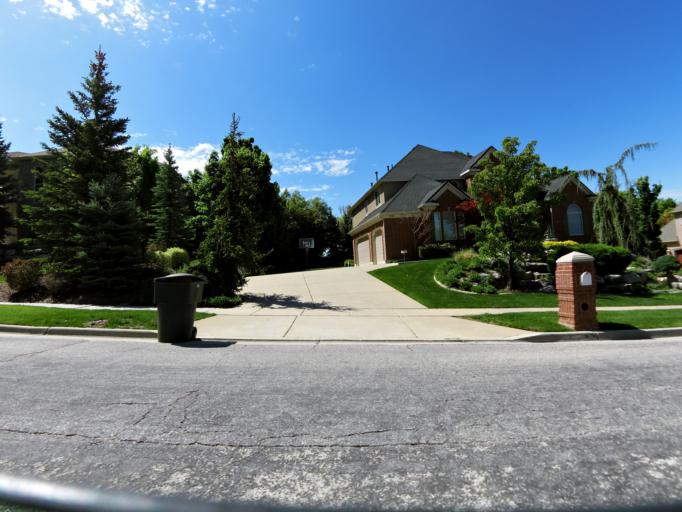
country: US
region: Utah
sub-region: Weber County
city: Uintah
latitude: 41.1729
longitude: -111.9385
